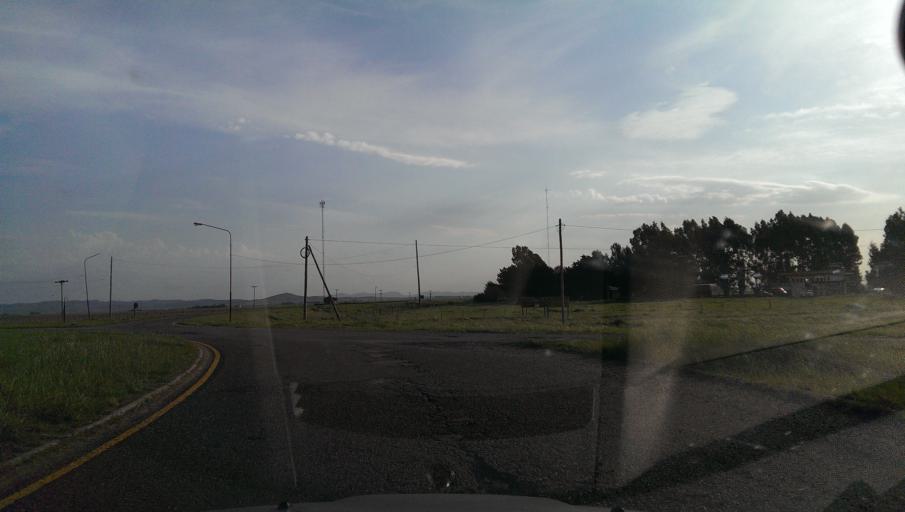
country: AR
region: Buenos Aires
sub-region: Partido de Coronel Suarez
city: Coronel Suarez
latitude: -37.7741
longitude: -61.7127
